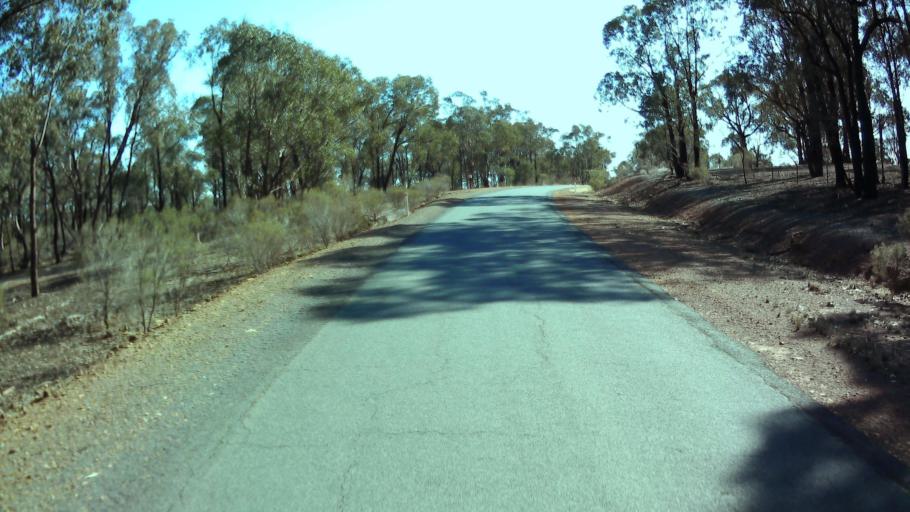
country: AU
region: New South Wales
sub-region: Weddin
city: Grenfell
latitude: -33.7836
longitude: 147.9595
